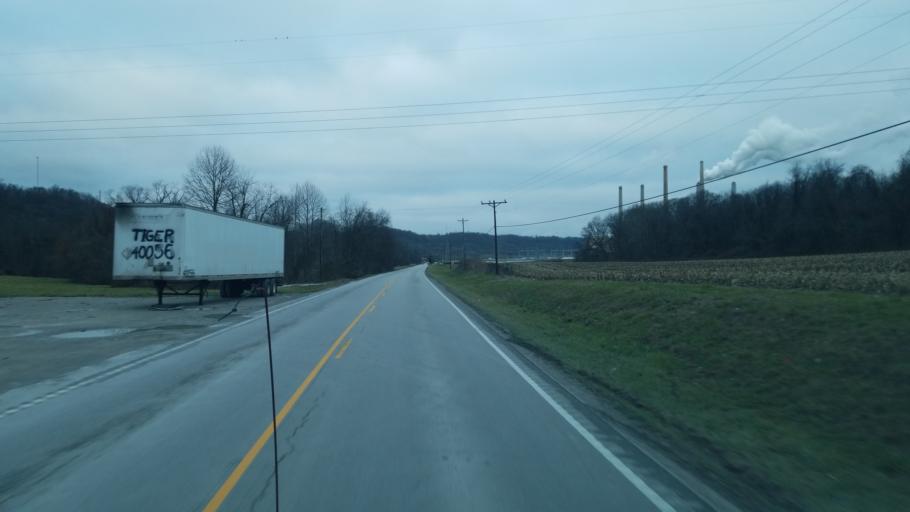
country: US
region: Ohio
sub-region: Brown County
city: Aberdeen
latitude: 38.6893
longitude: -83.7994
